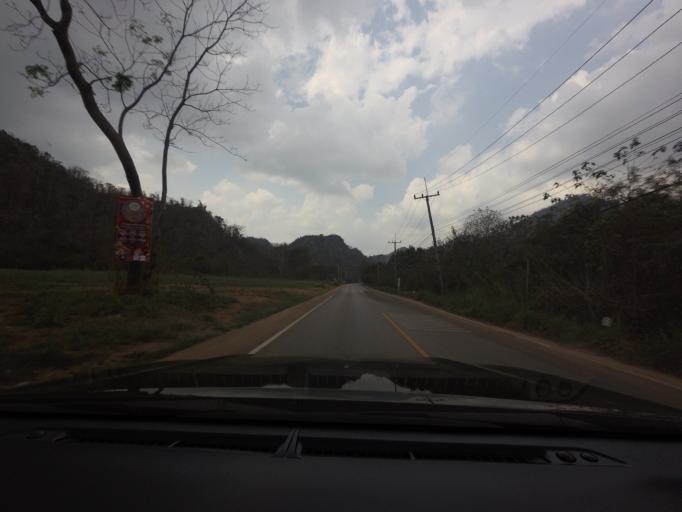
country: TH
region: Sara Buri
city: Muak Lek
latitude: 14.5702
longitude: 101.2921
